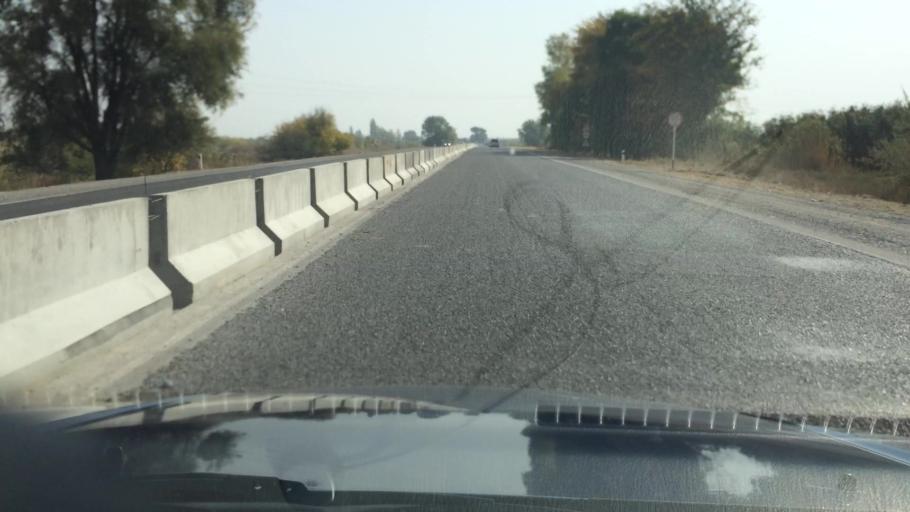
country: KG
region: Chuy
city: Kant
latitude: 42.9622
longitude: 74.9186
